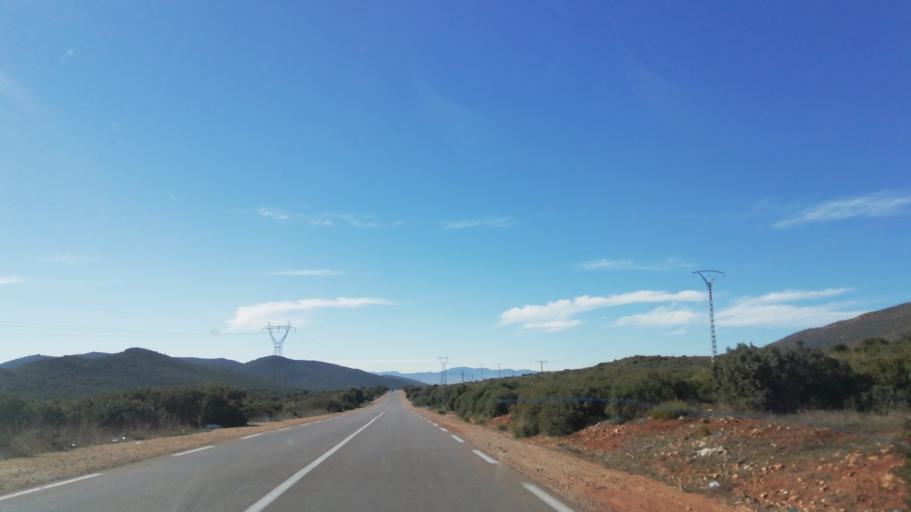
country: DZ
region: Tlemcen
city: Sebdou
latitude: 34.7188
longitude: -1.2018
